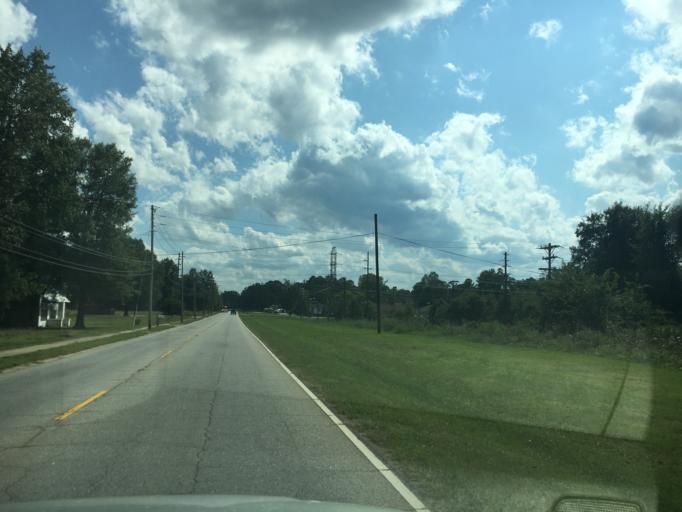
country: US
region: South Carolina
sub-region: Anderson County
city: Belton
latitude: 34.5341
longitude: -82.4954
